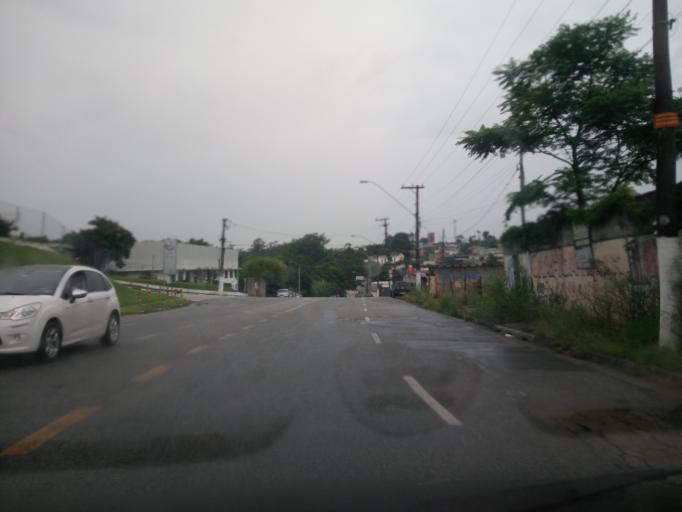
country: BR
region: Sao Paulo
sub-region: Sao Bernardo Do Campo
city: Sao Bernardo do Campo
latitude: -23.7671
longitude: -46.5936
